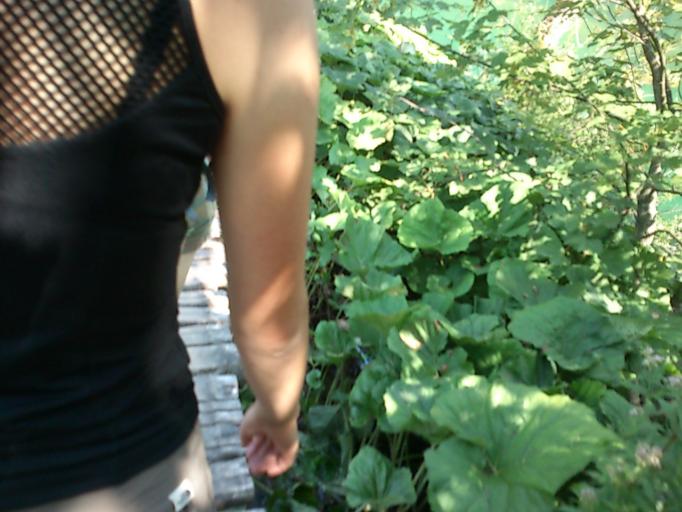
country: HR
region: Licko-Senjska
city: Jezerce
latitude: 44.8740
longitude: 15.6023
